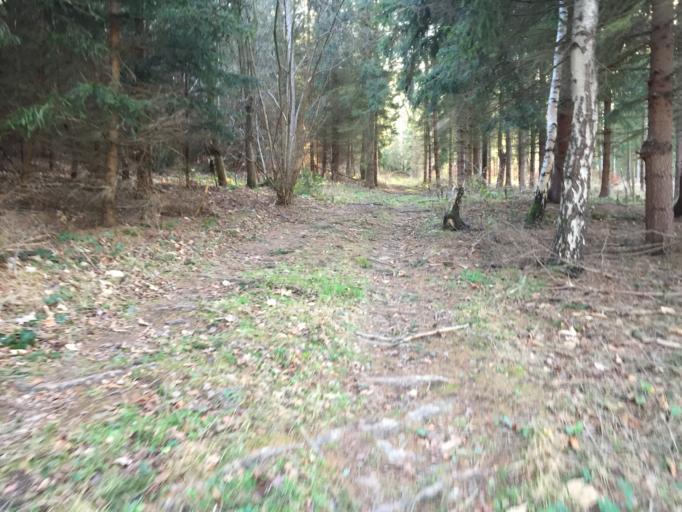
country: DE
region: Thuringia
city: Wernburg
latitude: 50.6626
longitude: 11.5954
